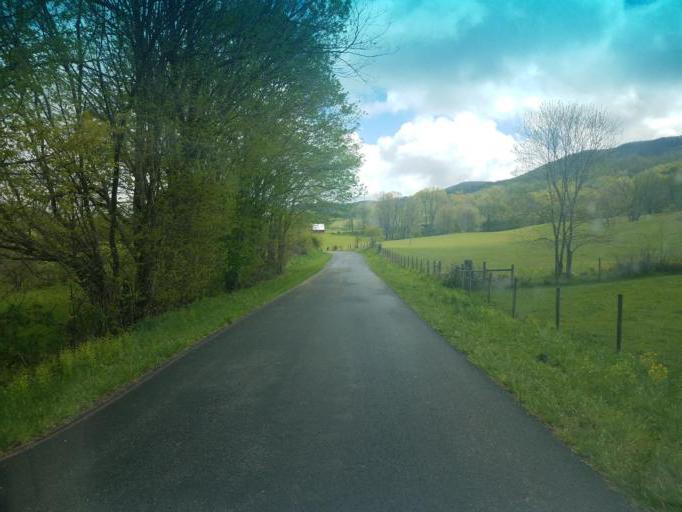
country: US
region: Virginia
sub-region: Smyth County
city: Atkins
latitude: 36.9423
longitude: -81.4186
